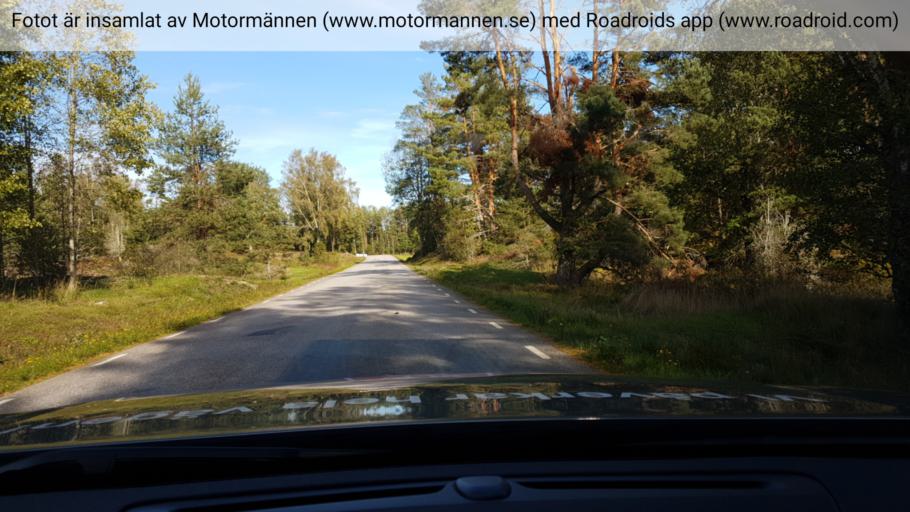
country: SE
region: OEstergoetland
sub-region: Valdemarsviks Kommun
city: Valdemarsvik
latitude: 58.0656
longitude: 16.6401
